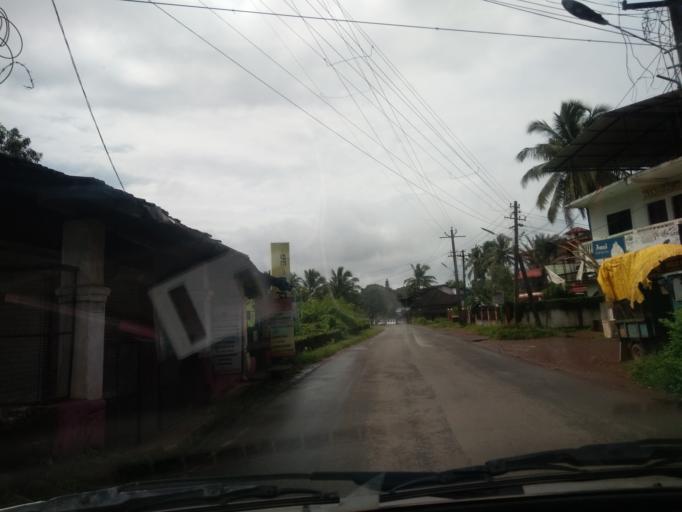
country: IN
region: Goa
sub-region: South Goa
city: Davorlim
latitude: 15.2922
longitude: 74.0064
